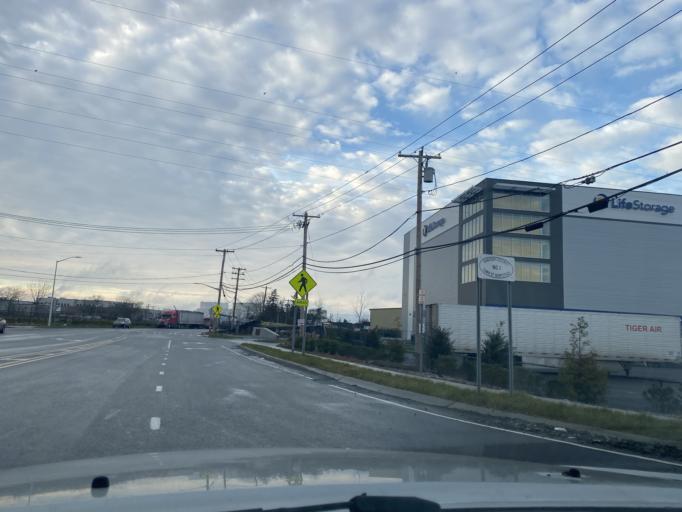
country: US
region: New York
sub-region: Nassau County
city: Inwood
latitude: 40.6282
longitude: -73.7400
